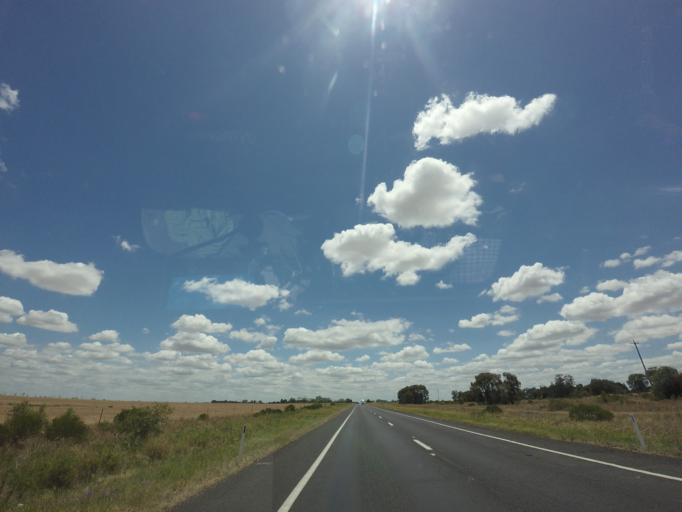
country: AU
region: New South Wales
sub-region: Moree Plains
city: Boggabilla
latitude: -28.7845
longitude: 150.2568
